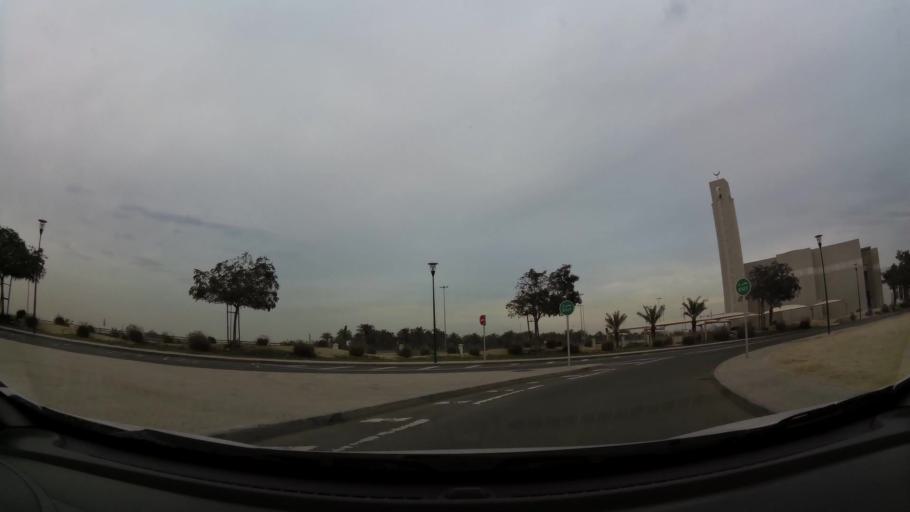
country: BH
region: Northern
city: Ar Rifa'
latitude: 26.1023
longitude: 50.5634
